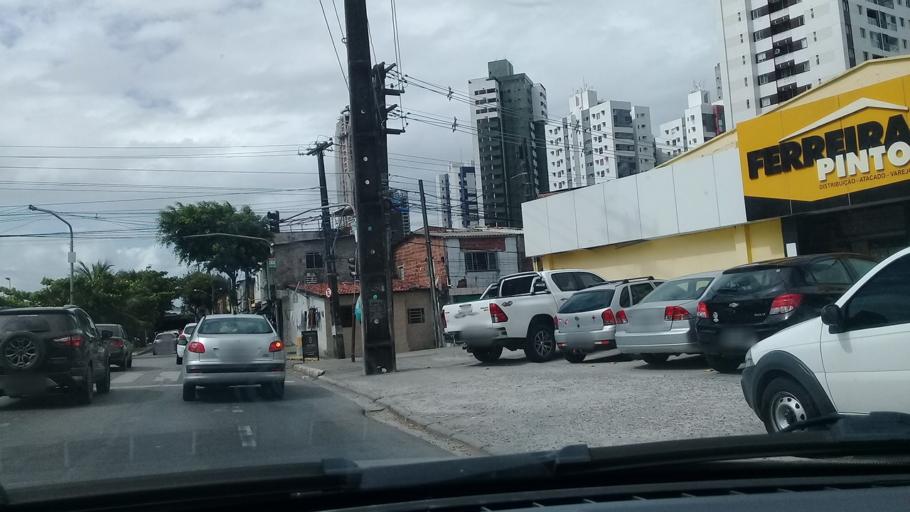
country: BR
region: Pernambuco
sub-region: Recife
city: Recife
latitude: -8.1271
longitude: -34.9099
